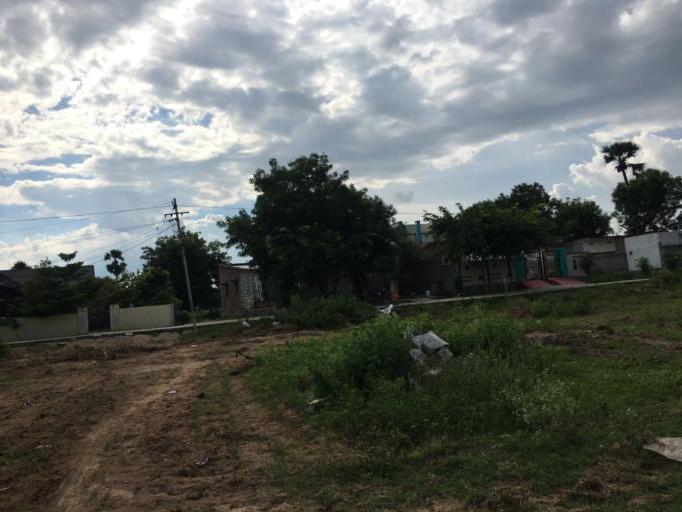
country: IN
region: Telangana
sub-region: Nalgonda
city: Nalgonda
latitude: 17.1688
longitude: 79.4188
